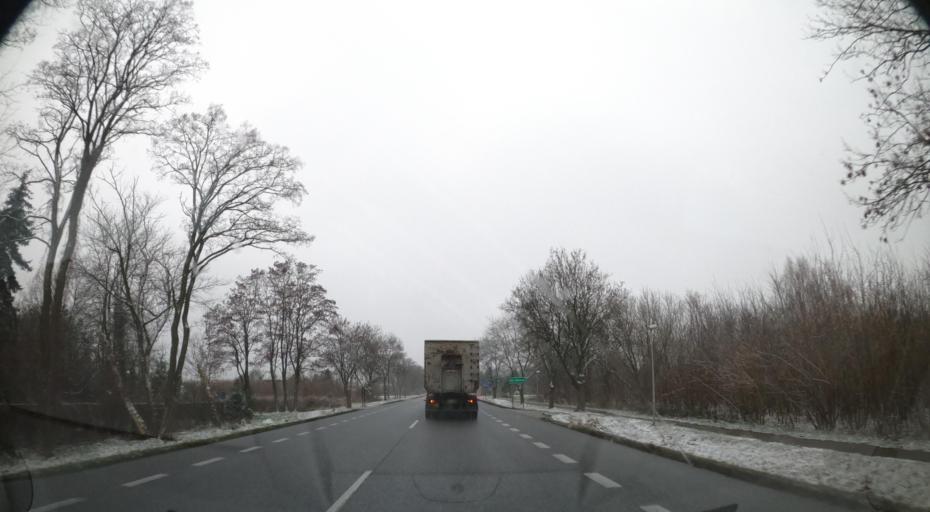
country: PL
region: Masovian Voivodeship
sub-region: Powiat sochaczewski
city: Teresin
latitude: 52.2179
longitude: 20.3652
